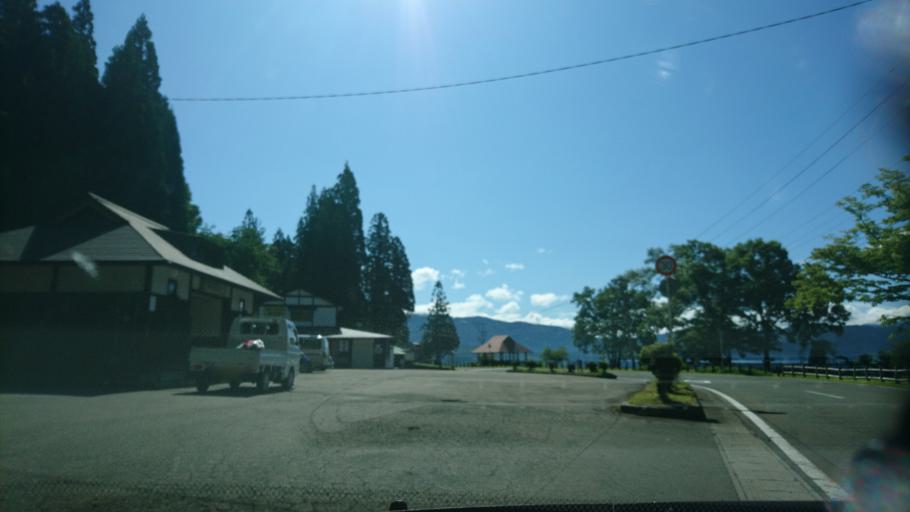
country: JP
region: Akita
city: Kakunodatemachi
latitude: 39.7514
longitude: 140.6492
